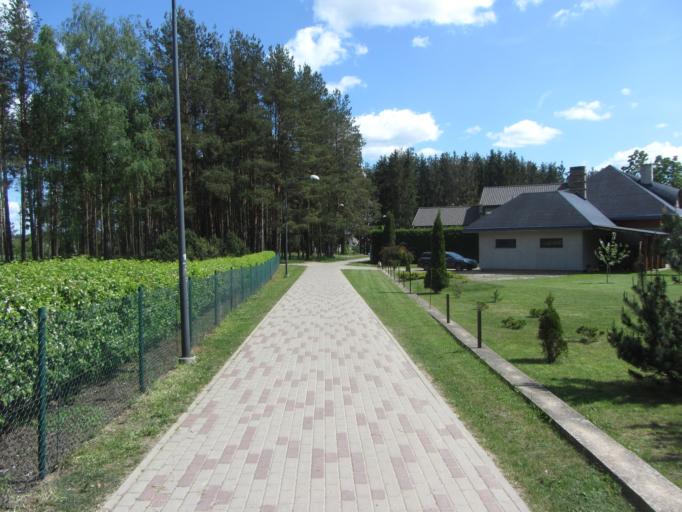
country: LT
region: Utenos apskritis
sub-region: Utena
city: Utena
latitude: 55.5049
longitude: 25.5921
